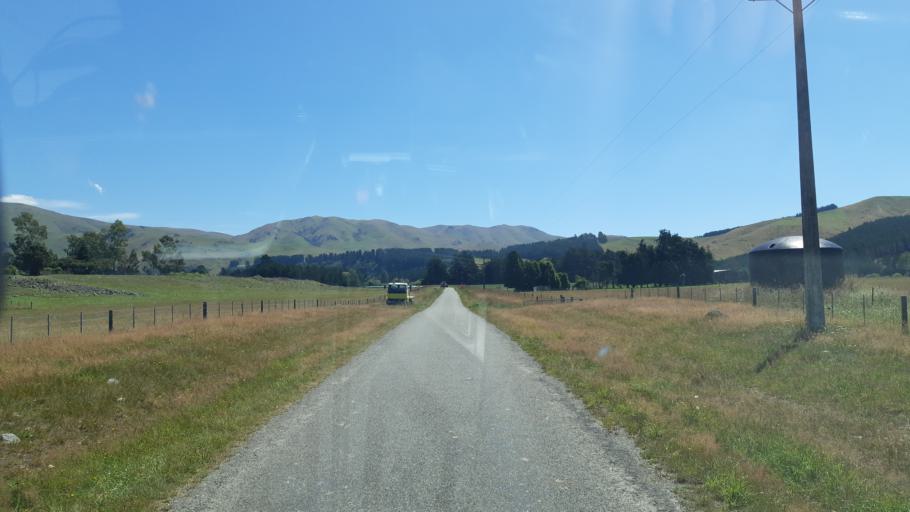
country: NZ
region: Canterbury
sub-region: Timaru District
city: Pleasant Point
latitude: -44.3339
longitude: 170.8870
